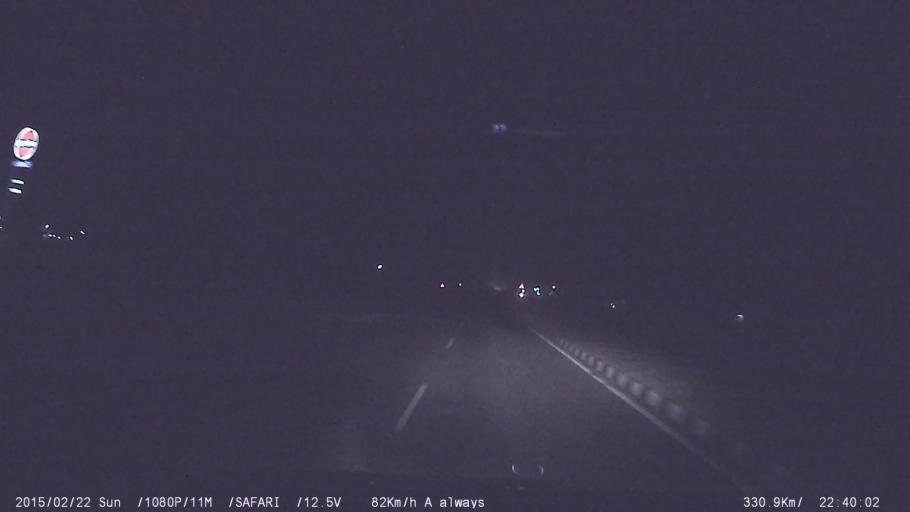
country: IN
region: Tamil Nadu
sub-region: Namakkal
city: Velur
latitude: 11.1751
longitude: 78.0533
